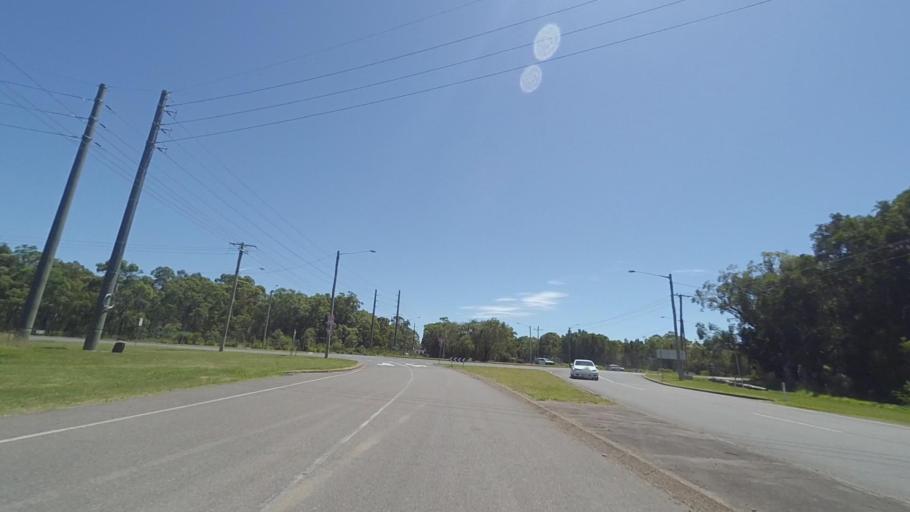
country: AU
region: New South Wales
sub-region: Port Stephens Shire
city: Medowie
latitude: -32.7728
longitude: 151.8596
